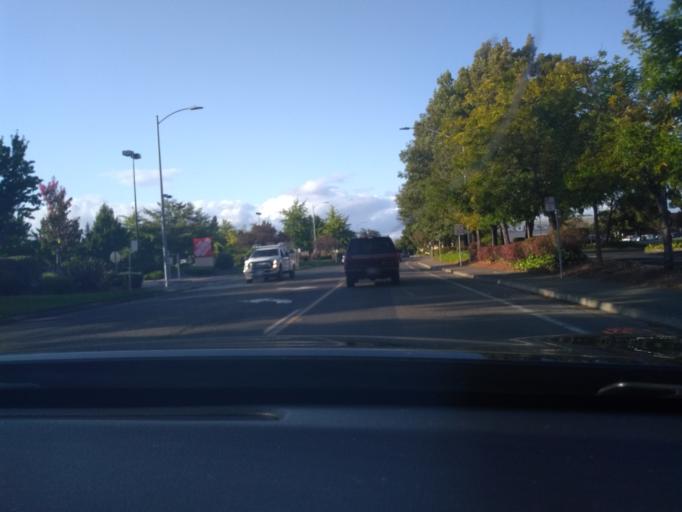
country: US
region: California
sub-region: Mendocino County
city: Ukiah
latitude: 39.1539
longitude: -123.1991
